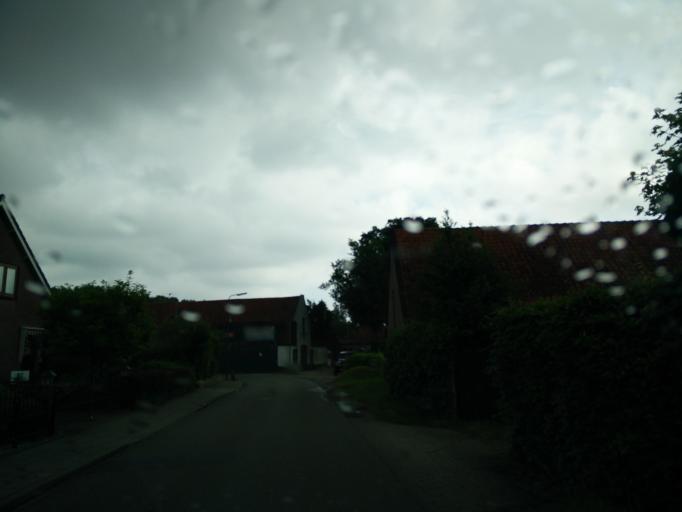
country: NL
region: Utrecht
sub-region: Gemeente Utrechtse Heuvelrug
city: Leersum
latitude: 52.0076
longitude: 5.4376
